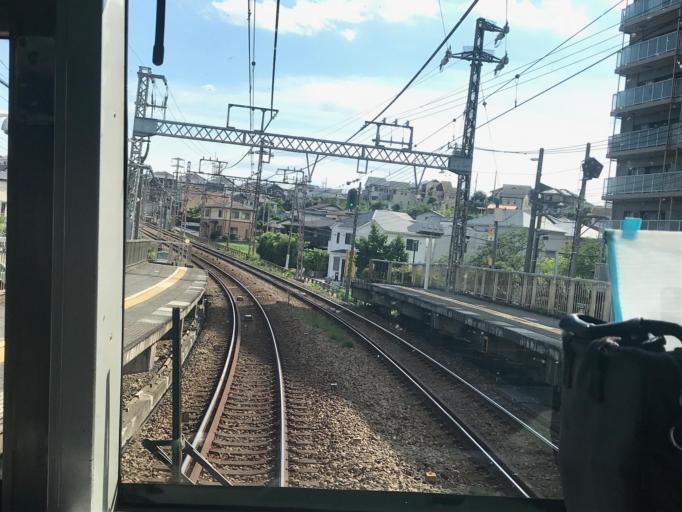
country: JP
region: Kanagawa
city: Isehara
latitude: 35.3804
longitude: 139.2767
